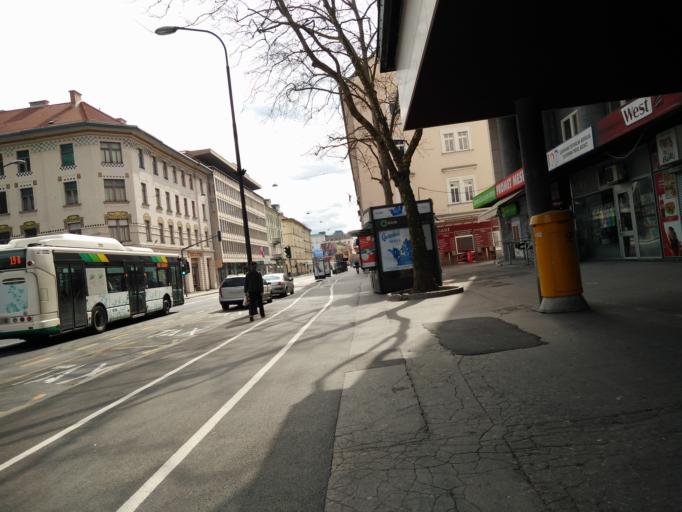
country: SI
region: Ljubljana
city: Ljubljana
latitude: 46.0563
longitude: 14.5052
